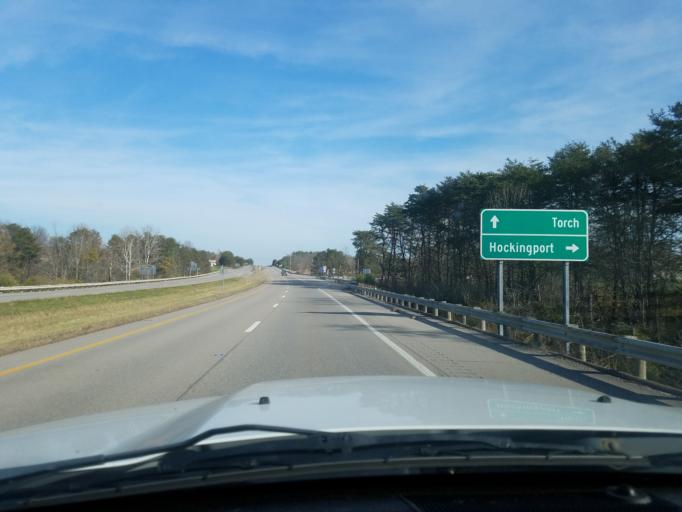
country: US
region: West Virginia
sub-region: Wood County
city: Washington
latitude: 39.2369
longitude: -81.7467
